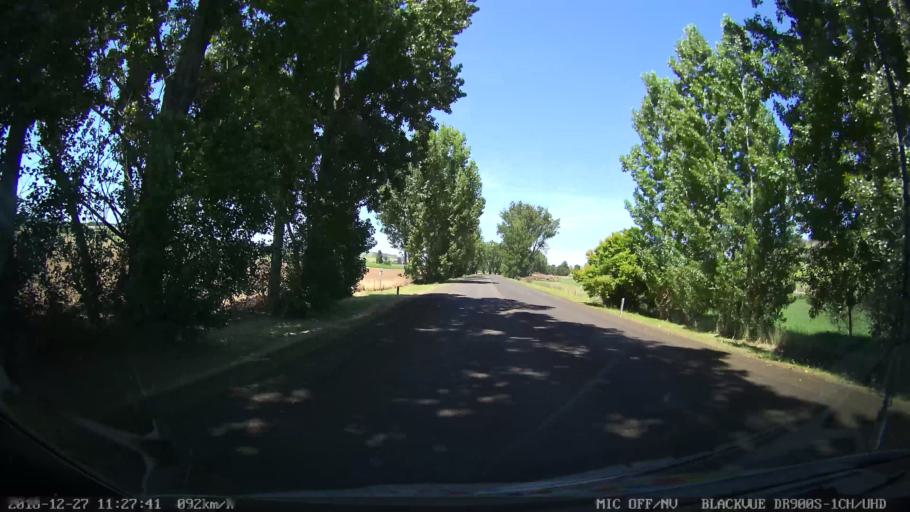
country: AU
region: New South Wales
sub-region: Bathurst Regional
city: Perthville
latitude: -33.4680
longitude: 149.5688
